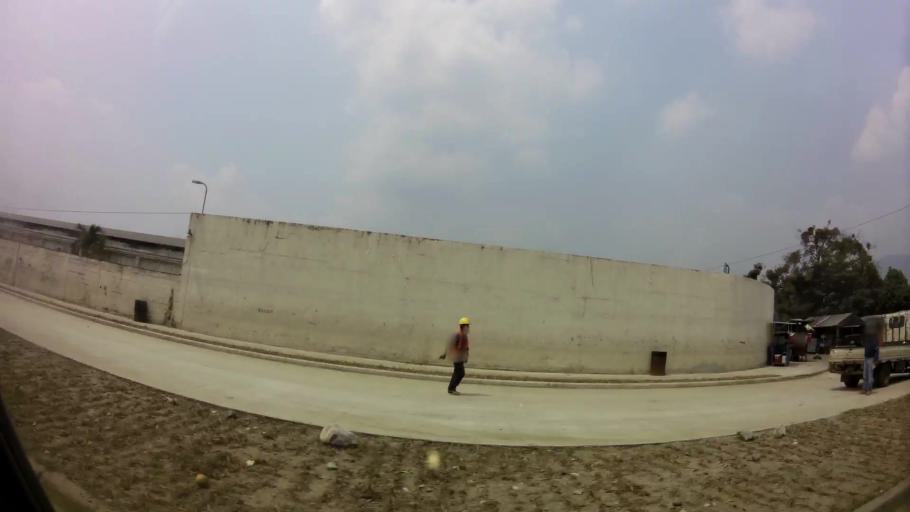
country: HN
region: Cortes
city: San Pedro Sula
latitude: 15.4835
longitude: -88.0267
